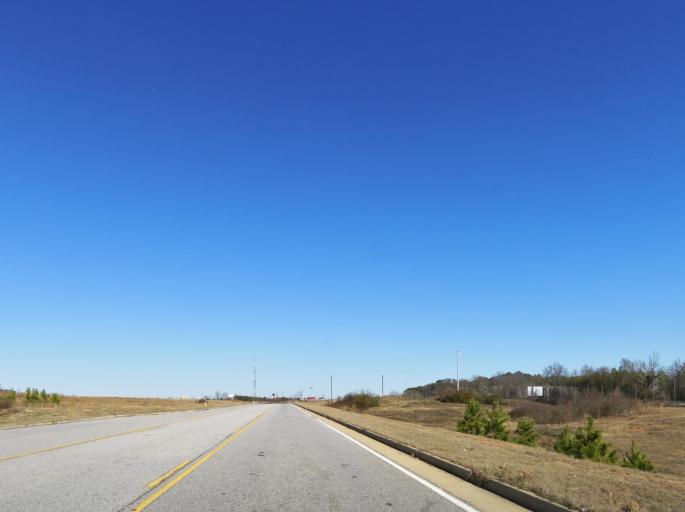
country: US
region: Georgia
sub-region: Peach County
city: Byron
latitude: 32.7321
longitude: -83.7253
